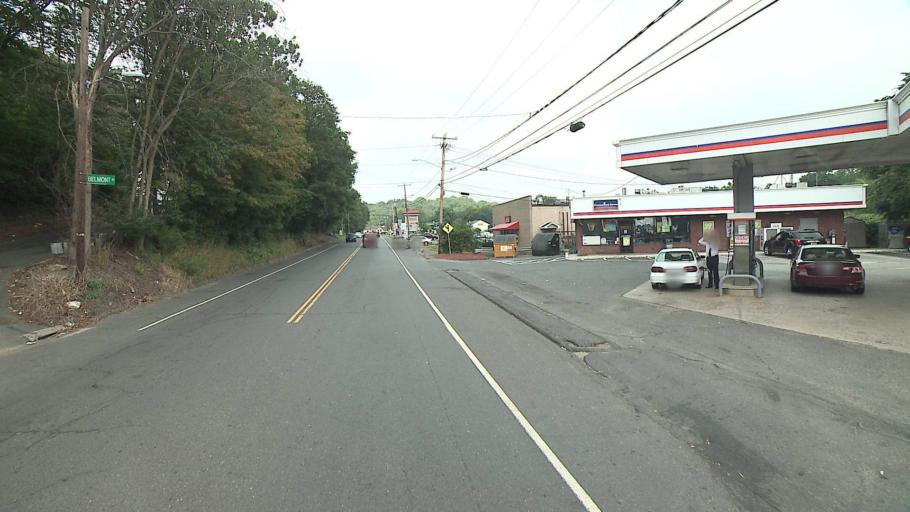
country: US
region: Connecticut
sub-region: Litchfield County
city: Oakville
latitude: 41.5839
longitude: -73.0747
